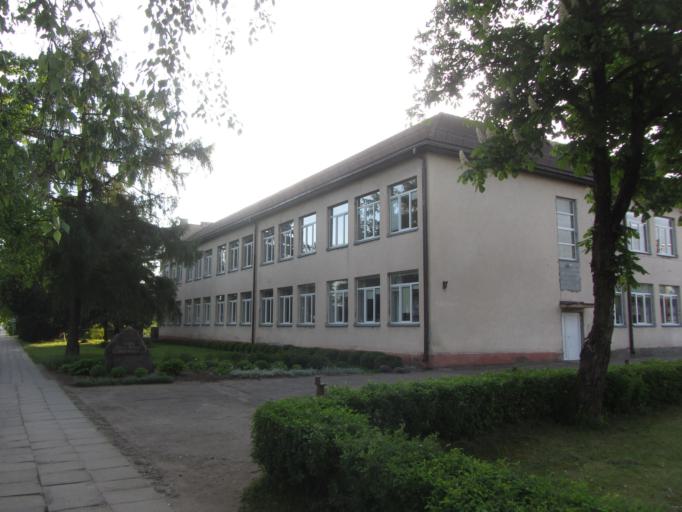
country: LT
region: Utenos apskritis
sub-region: Utena
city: Utena
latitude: 55.4966
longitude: 25.5916
